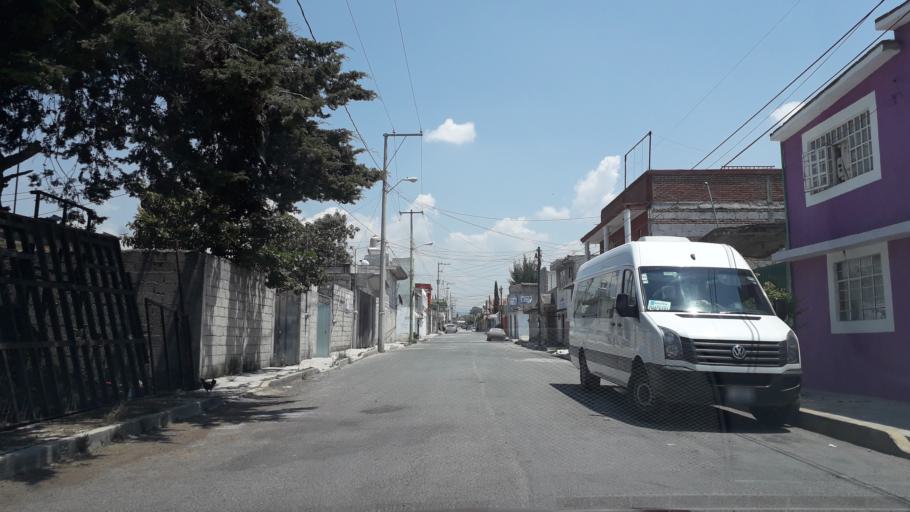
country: MX
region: Puebla
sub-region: Puebla
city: Primero de Mayo
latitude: 19.0688
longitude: -98.1208
